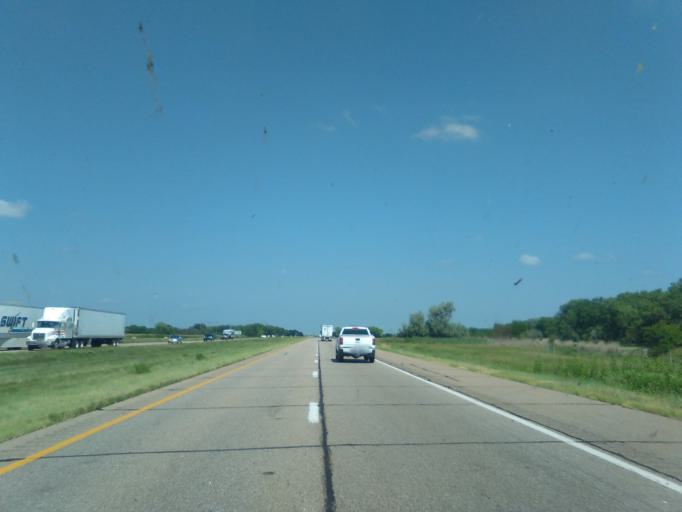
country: US
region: Nebraska
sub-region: Phelps County
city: Holdrege
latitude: 40.6907
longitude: -99.3595
